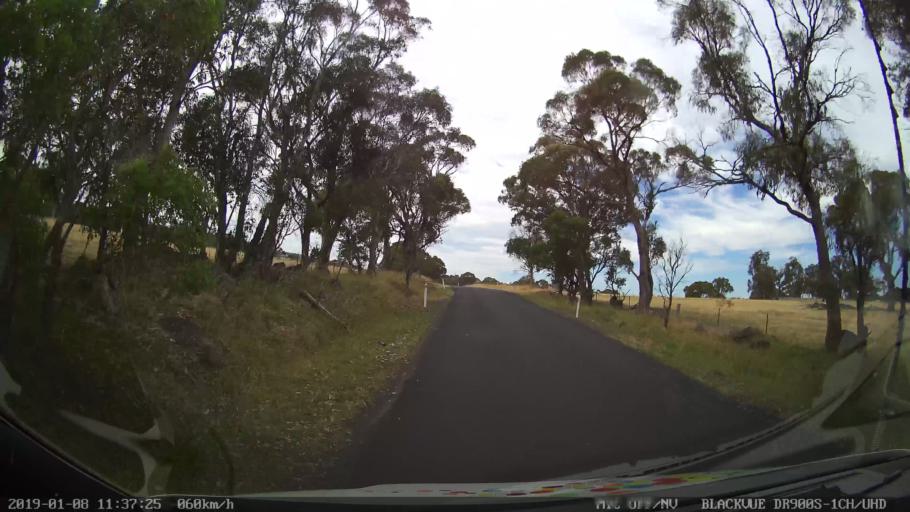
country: AU
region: New South Wales
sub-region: Guyra
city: Guyra
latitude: -30.3521
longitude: 151.5514
